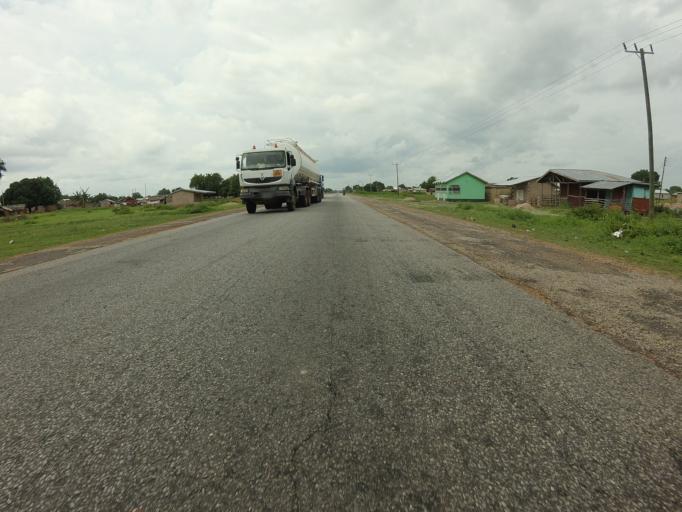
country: GH
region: Brong-Ahafo
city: Kintampo
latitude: 8.7355
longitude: -1.4722
